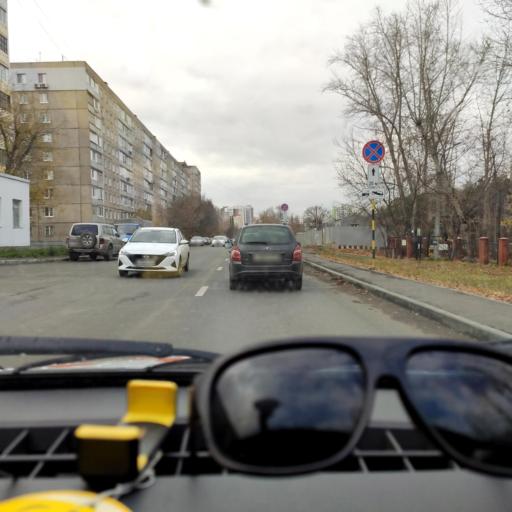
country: RU
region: Bashkortostan
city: Ufa
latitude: 54.7250
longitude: 56.0049
